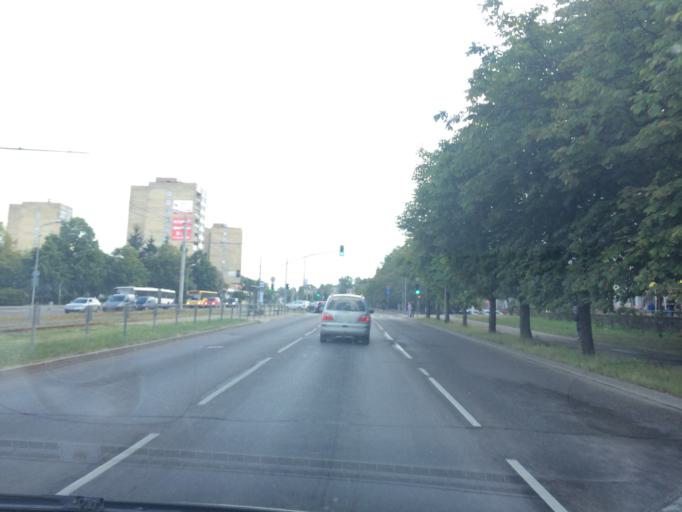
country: LV
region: Kekava
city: Balozi
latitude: 56.9157
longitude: 24.1747
